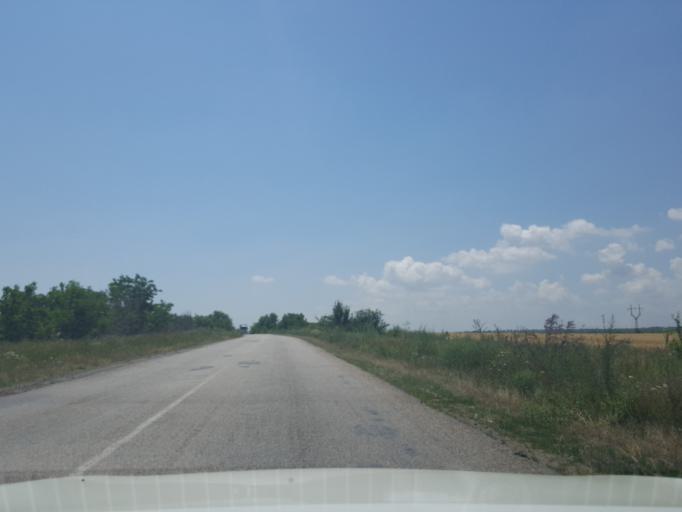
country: UA
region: Odessa
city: Starokozache
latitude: 46.3926
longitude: 30.0915
